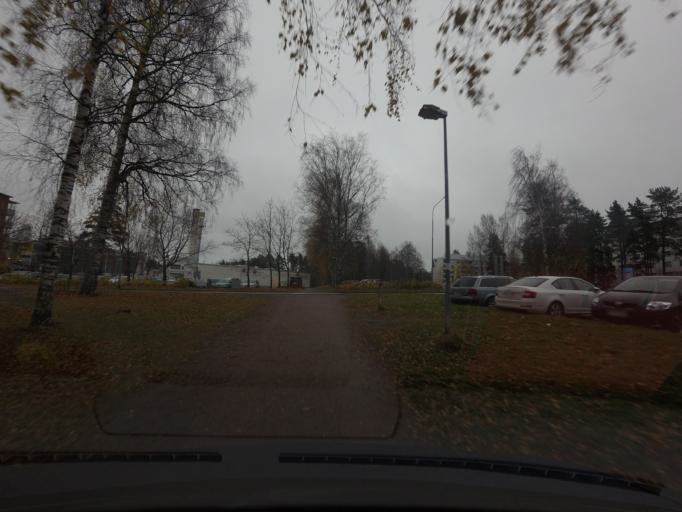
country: FI
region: Uusimaa
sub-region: Helsinki
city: Kilo
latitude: 60.2286
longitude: 24.7616
